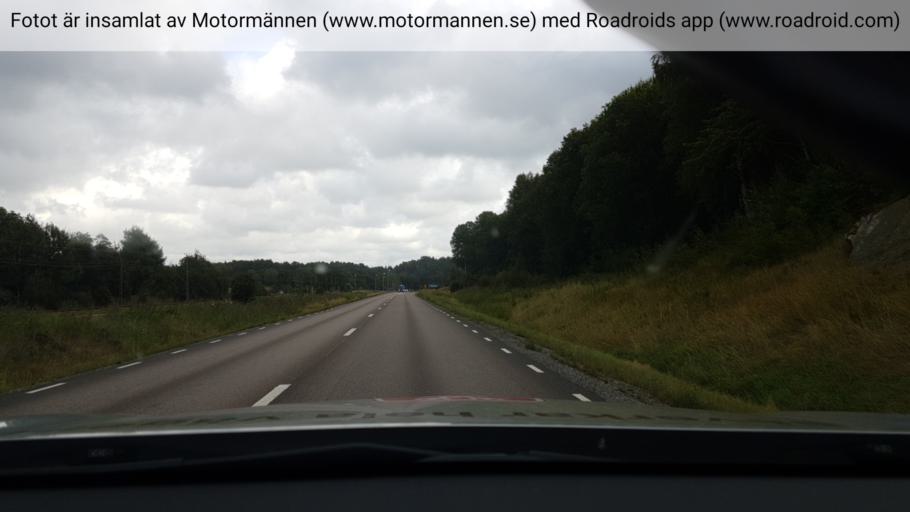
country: SE
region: Vaestra Goetaland
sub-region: Stromstads Kommun
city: Stroemstad
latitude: 58.9354
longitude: 11.2048
